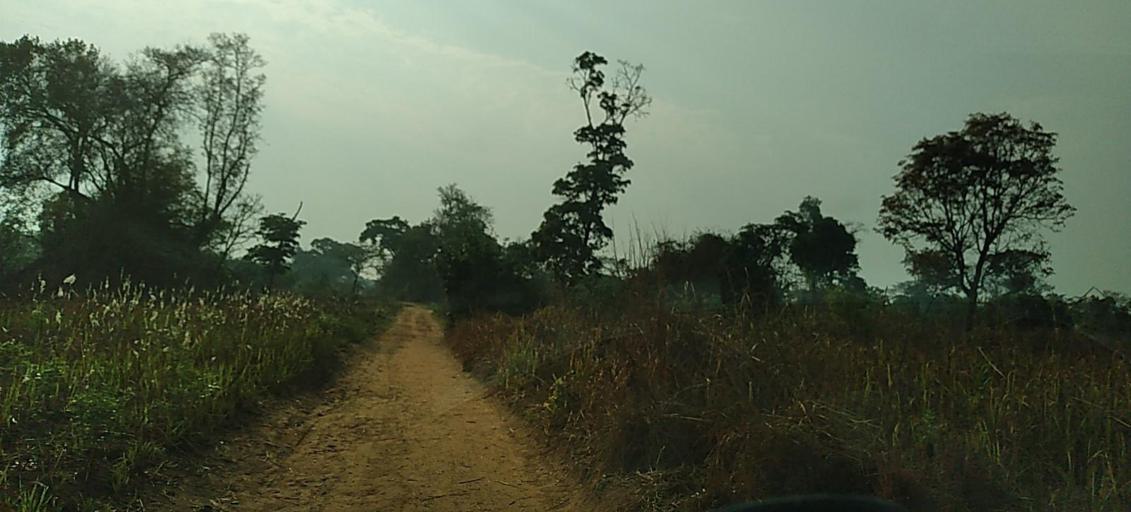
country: ZM
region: North-Western
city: Solwezi
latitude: -12.3533
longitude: 26.5384
